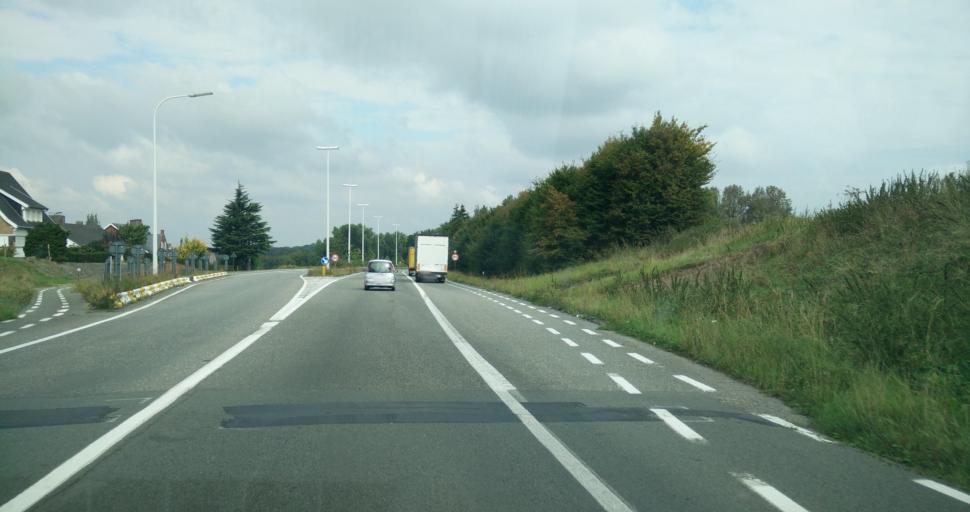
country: BE
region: Flanders
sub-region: Provincie Oost-Vlaanderen
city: Ronse
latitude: 50.7726
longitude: 3.5900
